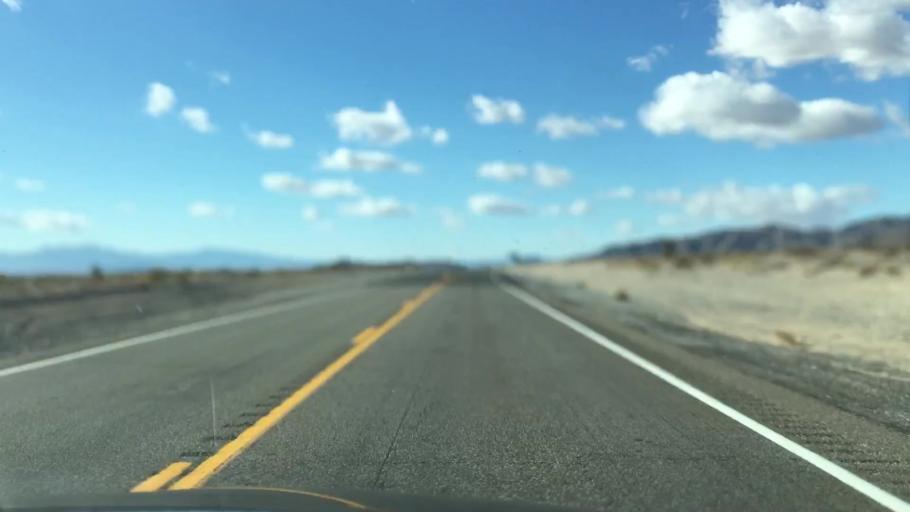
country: US
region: Nevada
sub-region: Nye County
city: Pahrump
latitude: 36.5641
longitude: -116.1184
